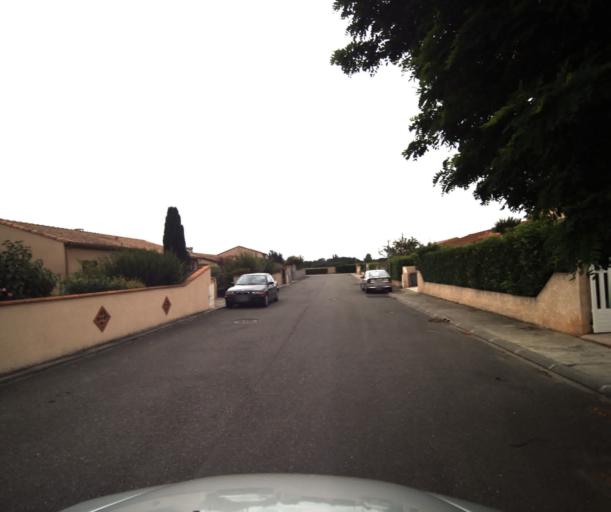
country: FR
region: Midi-Pyrenees
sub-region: Departement de la Haute-Garonne
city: Muret
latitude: 43.4552
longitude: 1.3161
